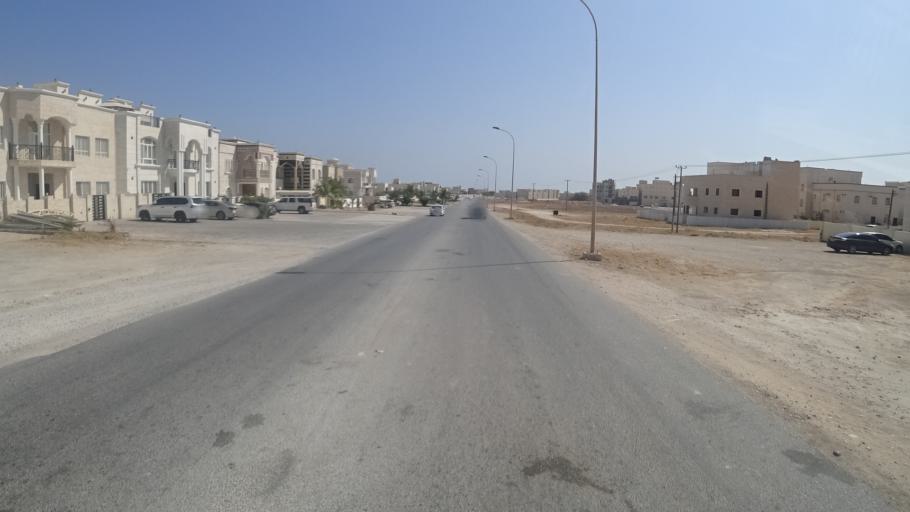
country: OM
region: Zufar
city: Salalah
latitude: 17.0139
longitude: 54.0230
